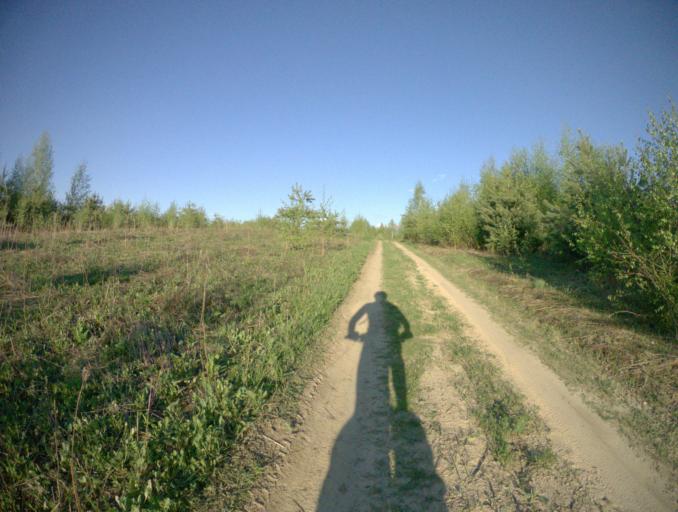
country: RU
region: Vladimir
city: Raduzhnyy
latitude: 55.9947
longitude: 40.2345
